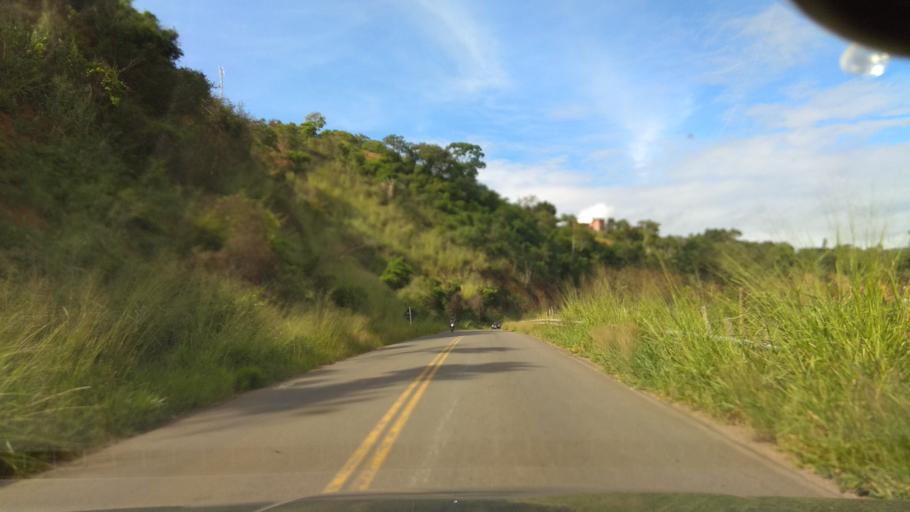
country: BR
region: Bahia
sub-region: Ubaira
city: Ubaira
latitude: -13.2558
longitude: -39.6637
